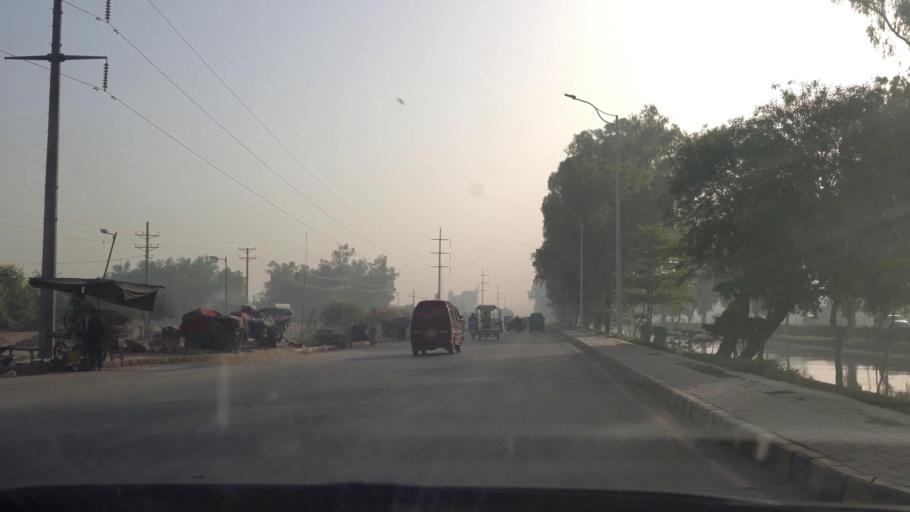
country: PK
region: Punjab
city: Faisalabad
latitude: 31.4515
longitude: 73.1507
